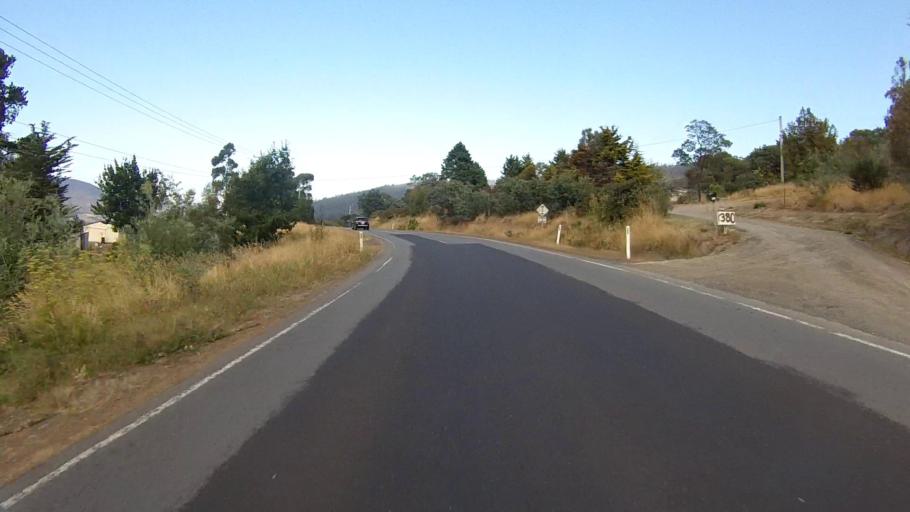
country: AU
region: Tasmania
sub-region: Brighton
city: Bridgewater
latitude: -42.7268
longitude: 147.1890
